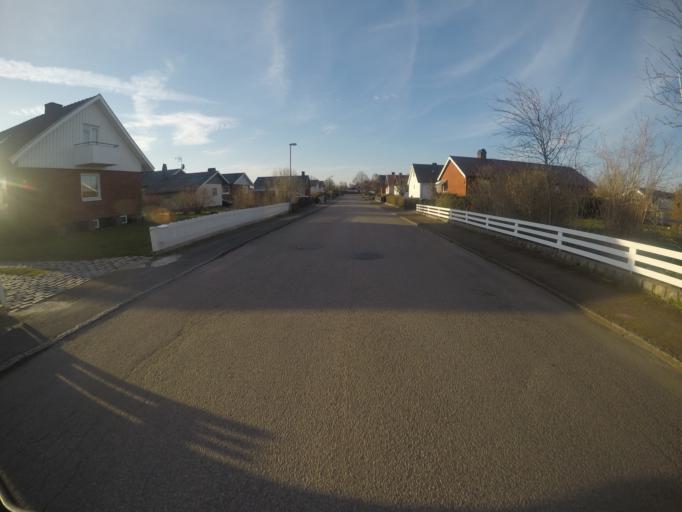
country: SE
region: Halland
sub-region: Laholms Kommun
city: Laholm
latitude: 56.5044
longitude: 13.0261
